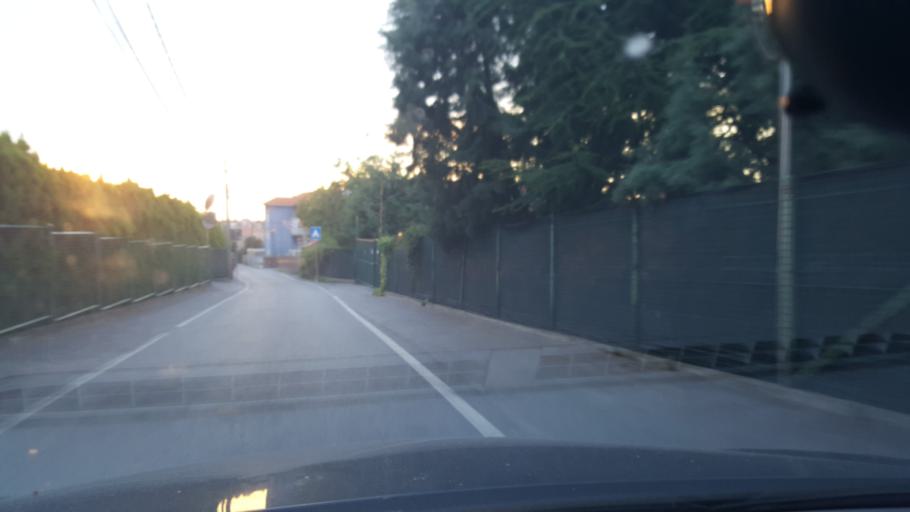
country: RS
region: Central Serbia
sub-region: Belgrade
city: Zvezdara
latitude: 44.7783
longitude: 20.5389
